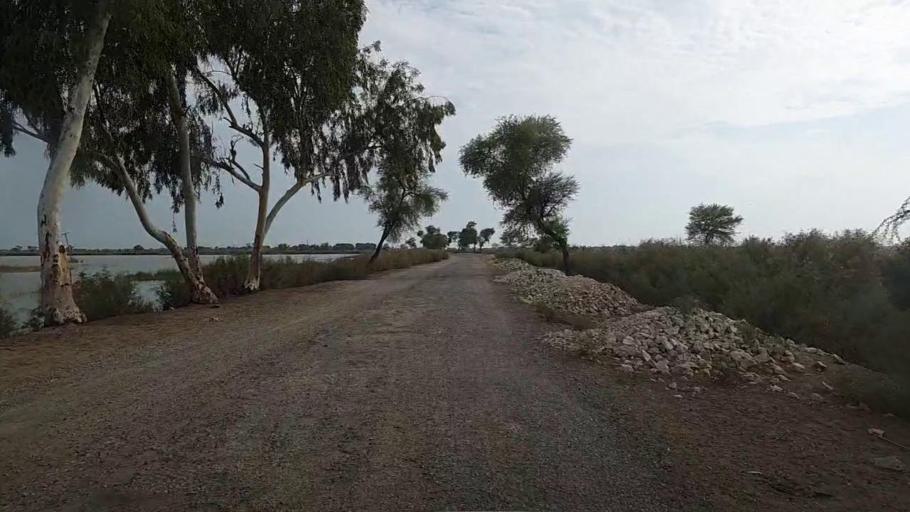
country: PK
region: Sindh
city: Thul
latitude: 28.2798
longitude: 68.8557
